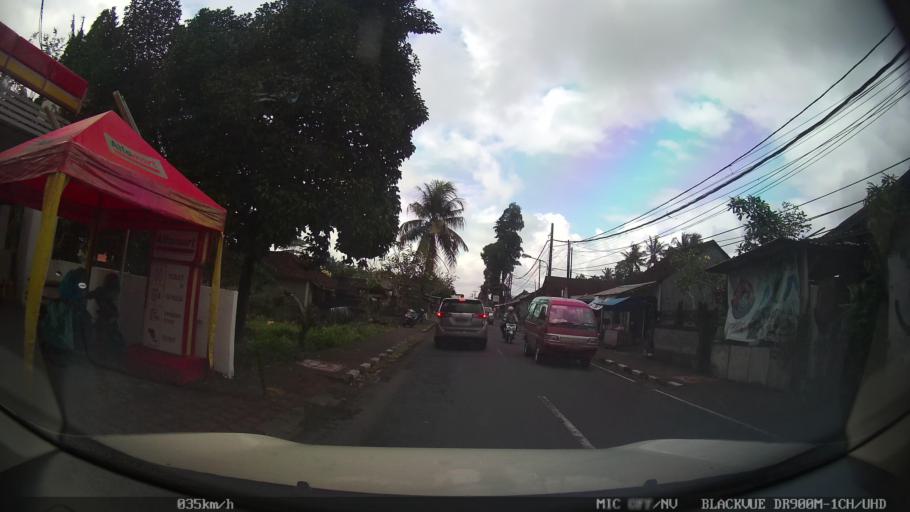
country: ID
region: Bali
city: Banjar Cemenggon
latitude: -8.5334
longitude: 115.2002
